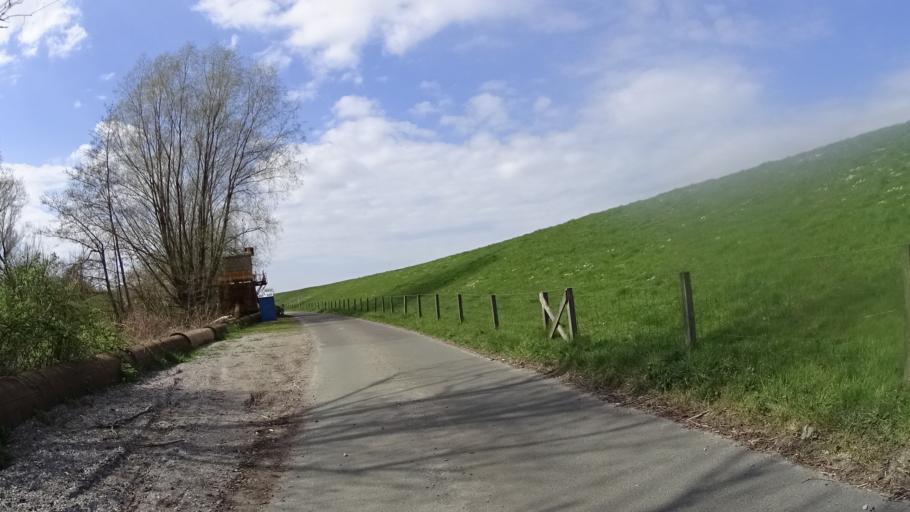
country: DE
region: Lower Saxony
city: Weener
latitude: 53.1036
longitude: 7.3255
